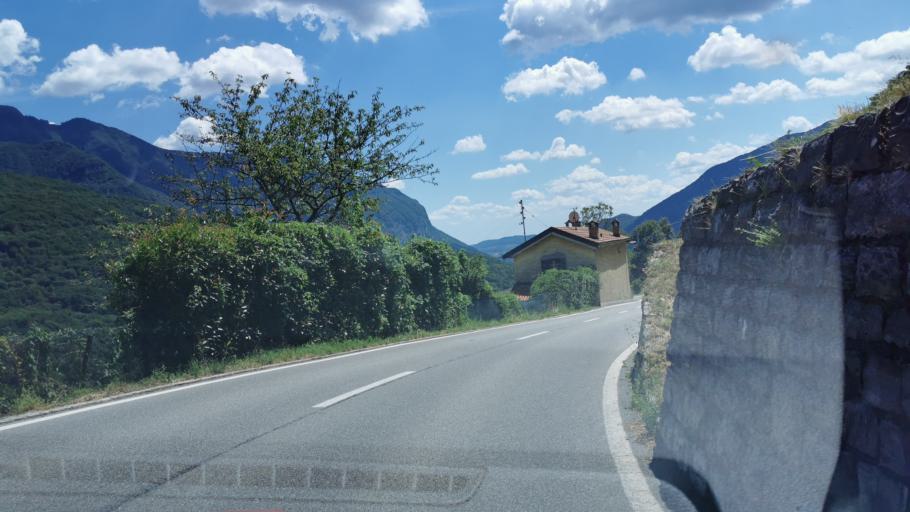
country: IT
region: Lombardy
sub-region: Provincia di Como
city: Campione
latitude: 45.9498
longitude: 8.9811
